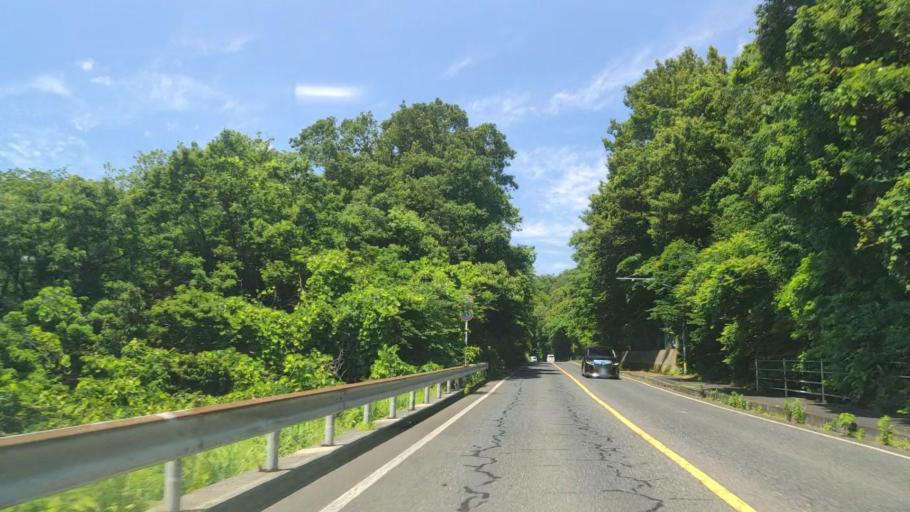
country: JP
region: Tottori
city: Tottori
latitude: 35.5261
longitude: 134.2303
